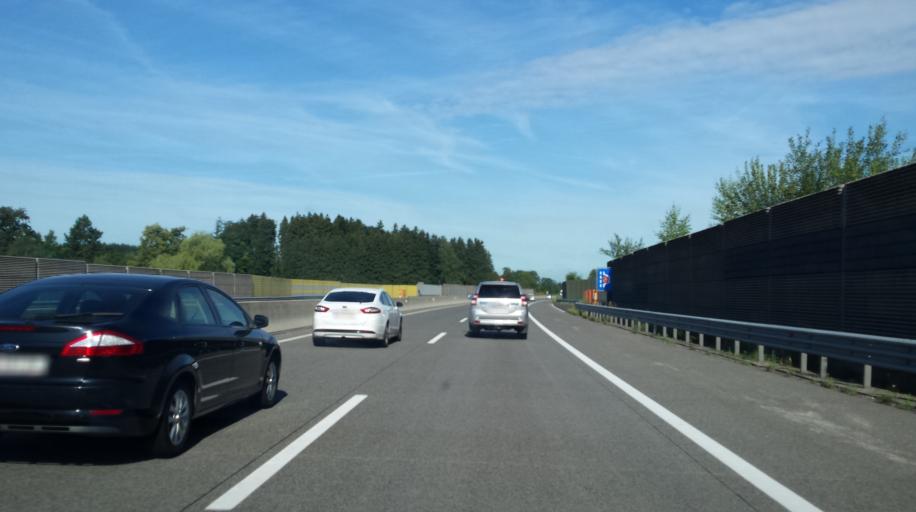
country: AT
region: Upper Austria
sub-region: Politischer Bezirk Vocklabruck
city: Aurach am Hongar
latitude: 47.9492
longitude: 13.6716
